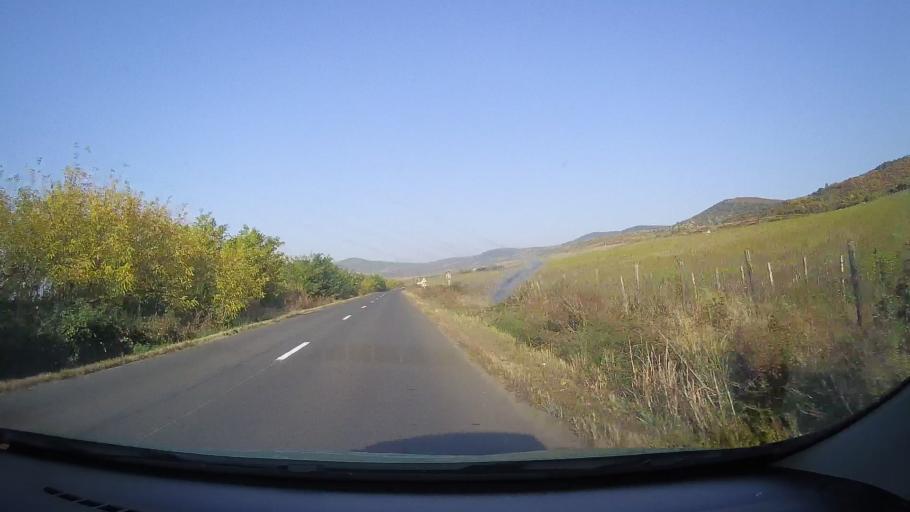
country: RO
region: Arad
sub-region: Comuna Covasint
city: Covasint
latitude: 46.2181
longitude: 21.6214
